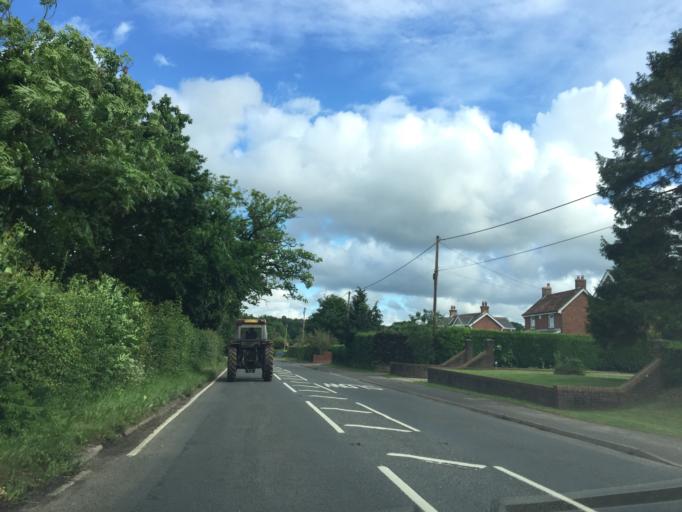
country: GB
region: England
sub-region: Hampshire
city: Cadnam
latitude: 50.9430
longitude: -1.5370
